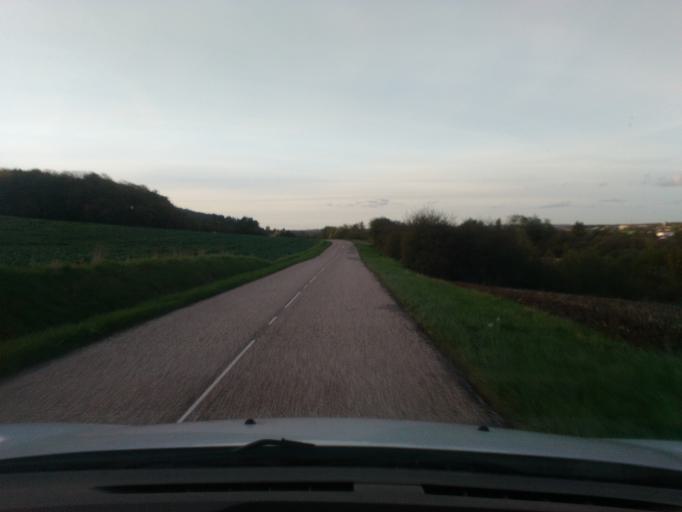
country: FR
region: Lorraine
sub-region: Departement des Vosges
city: Charmes
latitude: 48.3504
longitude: 6.3016
